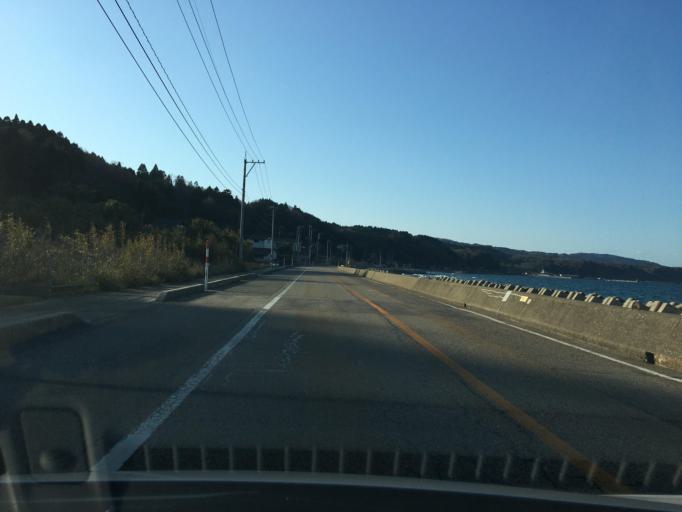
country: JP
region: Ishikawa
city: Nanao
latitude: 36.9960
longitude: 137.0520
